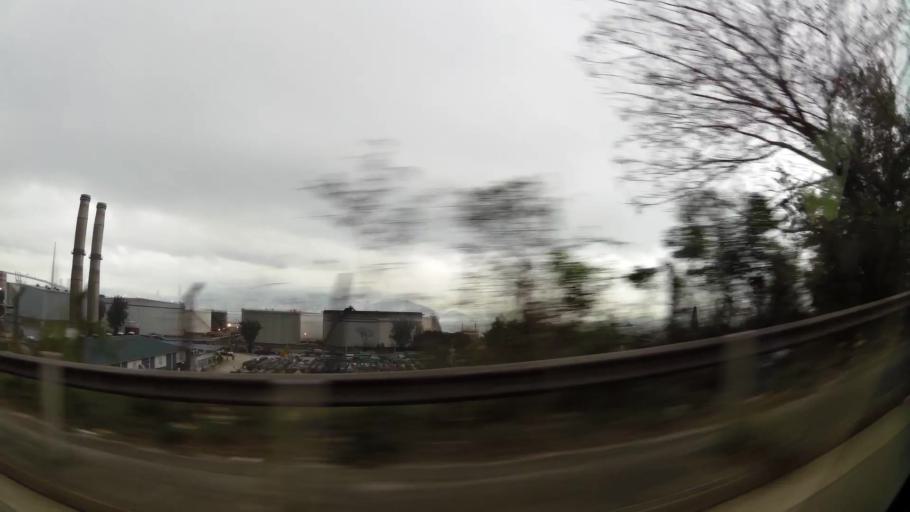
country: HK
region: Tsuen Wan
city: Tsuen Wan
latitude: 22.3316
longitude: 114.0987
